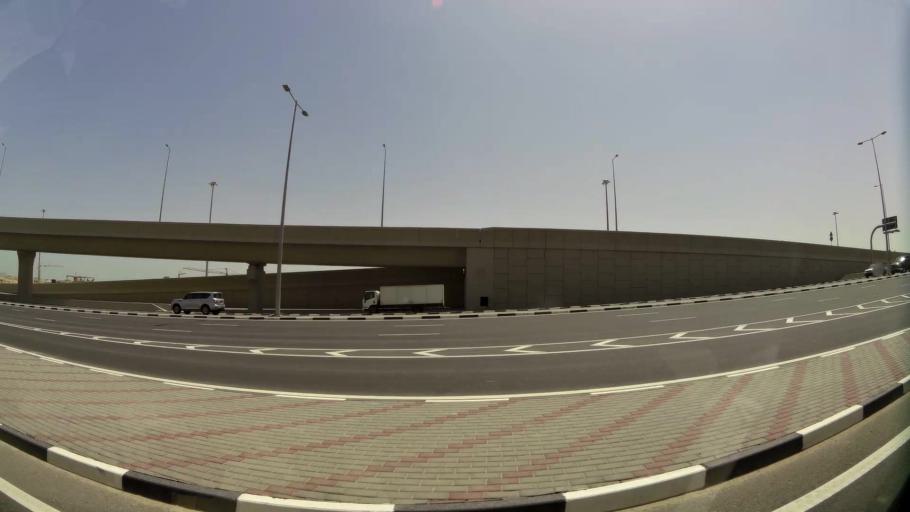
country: QA
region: Baladiyat Umm Salal
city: Umm Salal Muhammad
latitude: 25.3816
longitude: 51.4447
